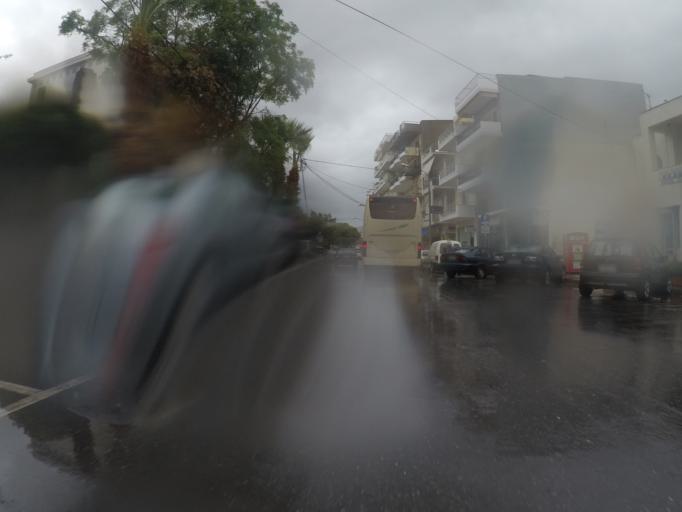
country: GR
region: Peloponnese
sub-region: Nomos Messinias
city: Messini
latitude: 37.0512
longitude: 22.0098
